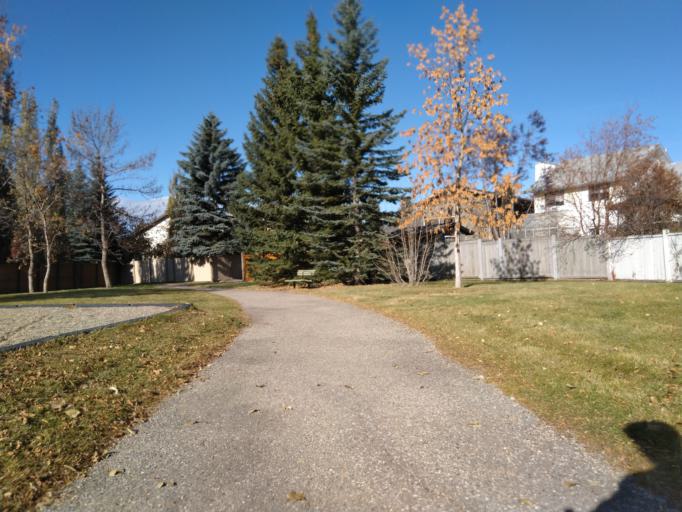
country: CA
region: Alberta
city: Calgary
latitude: 51.1365
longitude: -114.1539
